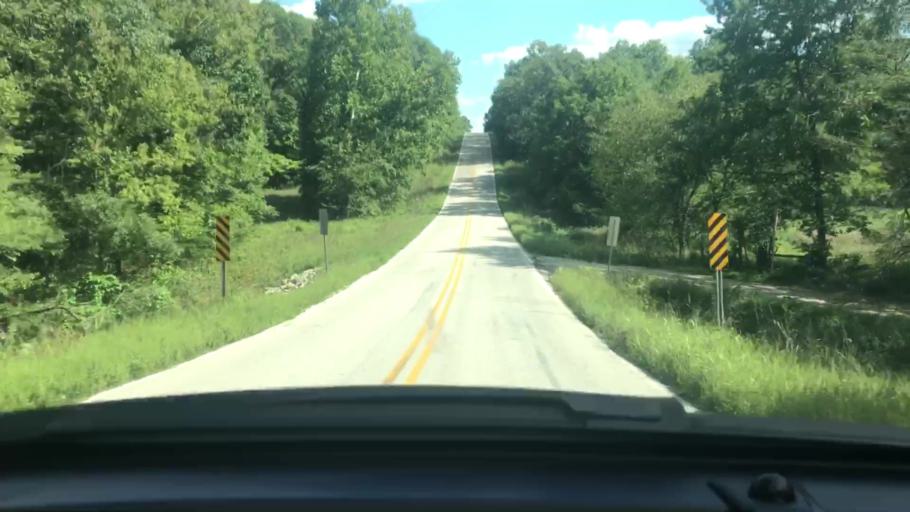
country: US
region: Missouri
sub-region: Wright County
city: Hartville
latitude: 37.3852
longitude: -92.4422
